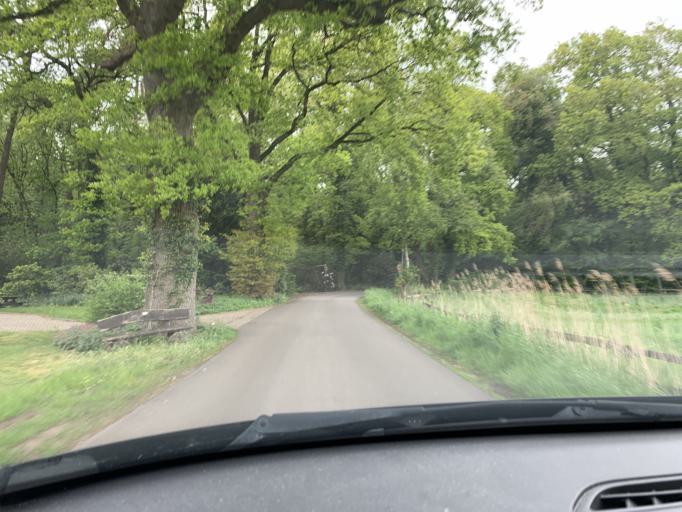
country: DE
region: Lower Saxony
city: Westerstede
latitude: 53.2444
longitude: 7.9142
